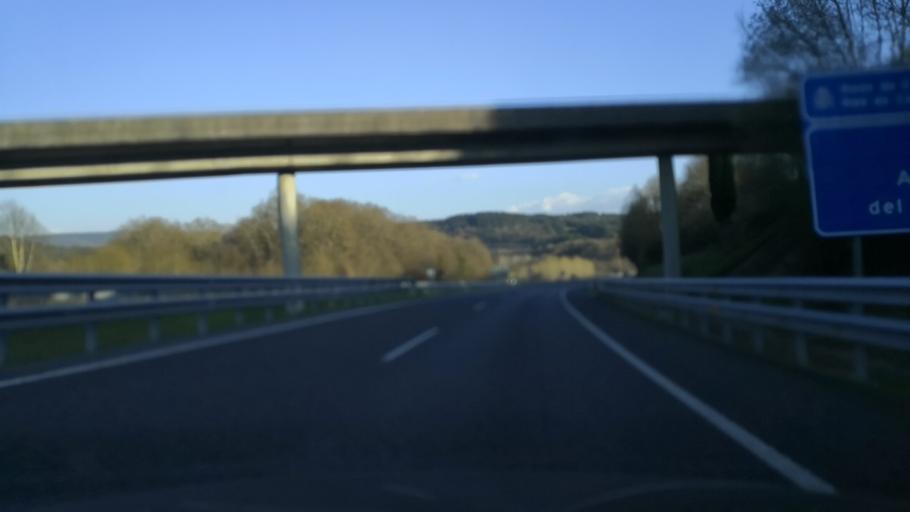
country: ES
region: Galicia
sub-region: Provincia de Lugo
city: Corgo
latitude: 42.9381
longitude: -7.3878
